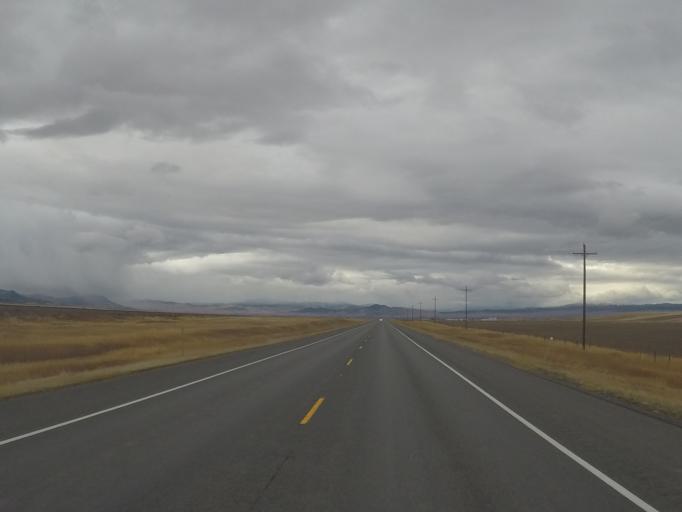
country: US
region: Montana
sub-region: Lewis and Clark County
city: East Helena
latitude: 46.5775
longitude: -111.8392
